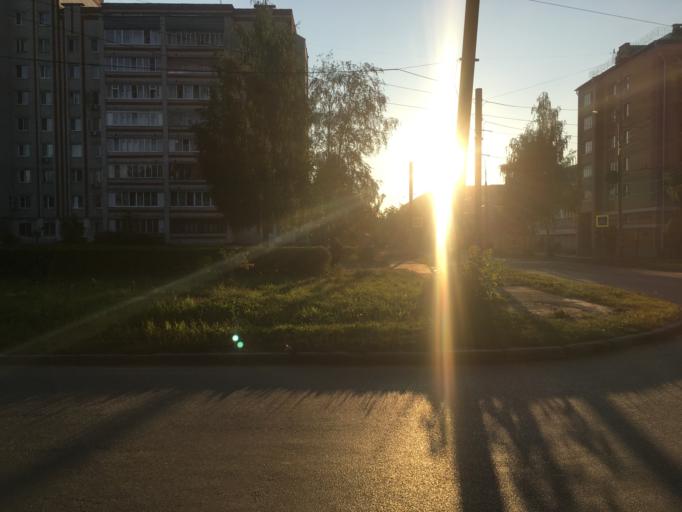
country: RU
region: Mariy-El
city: Yoshkar-Ola
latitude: 56.6505
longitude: 47.8749
